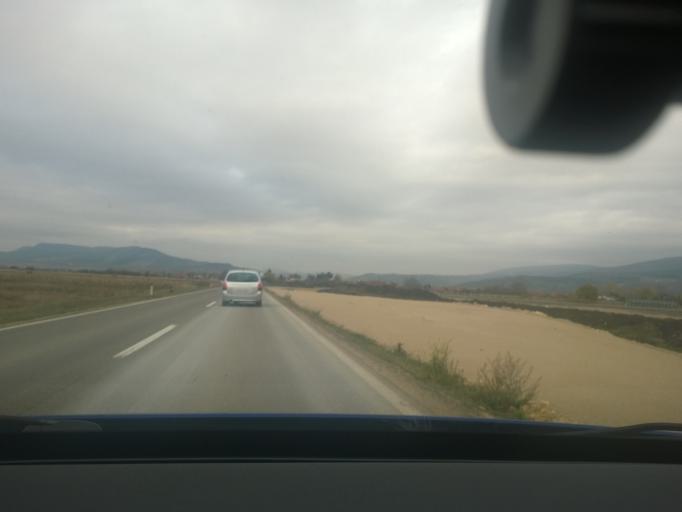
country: RS
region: Central Serbia
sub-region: Pirotski Okrug
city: Pirot
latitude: 43.1231
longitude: 22.6191
